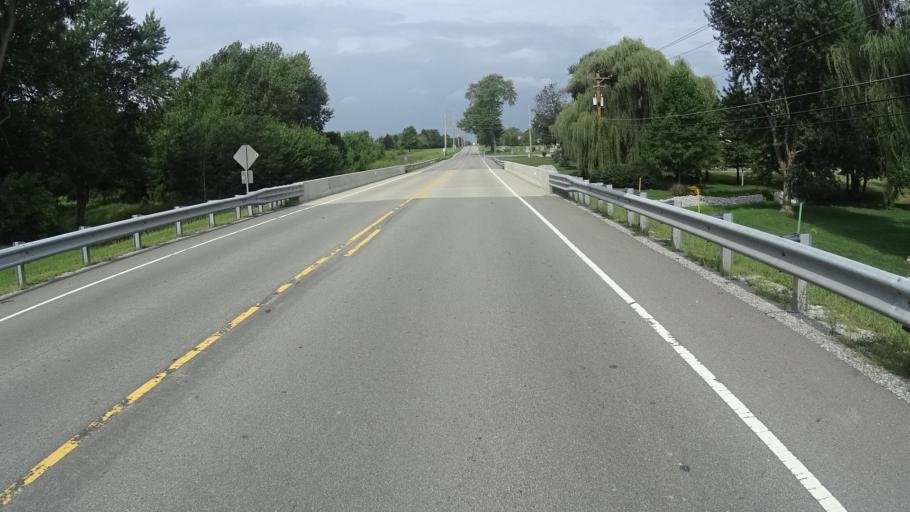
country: US
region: Indiana
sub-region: Madison County
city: Pendleton
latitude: 40.0096
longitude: -85.7895
